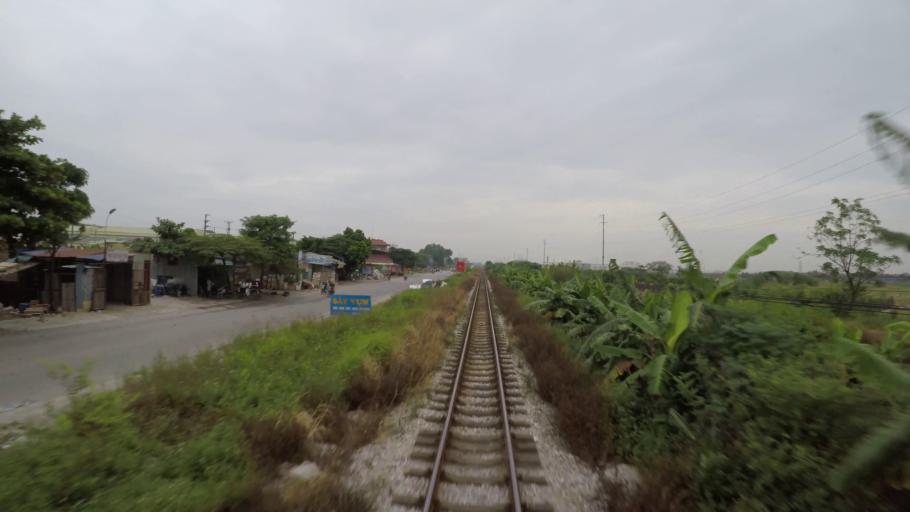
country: VN
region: Hung Yen
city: Nhu Quynh
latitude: 20.9834
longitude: 106.0317
